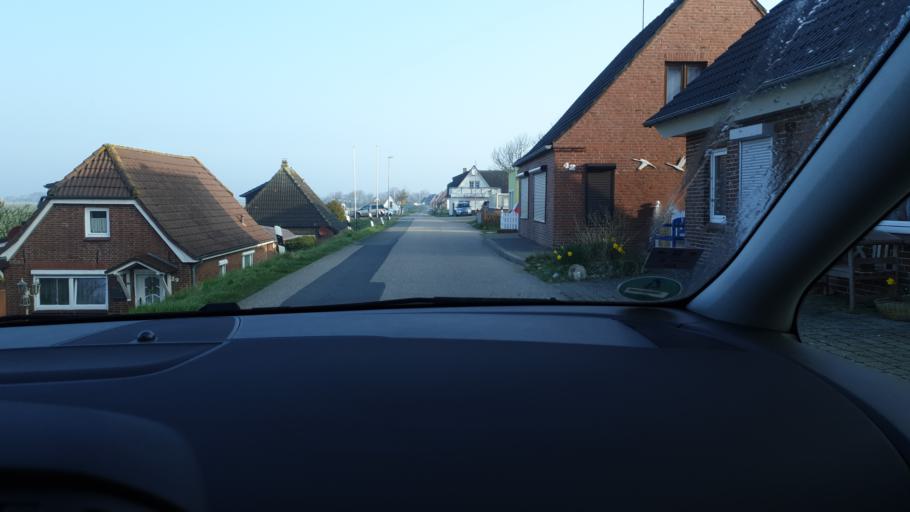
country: DE
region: Schleswig-Holstein
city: Elisabeth-Sophien-Koog
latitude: 54.4963
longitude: 8.8790
